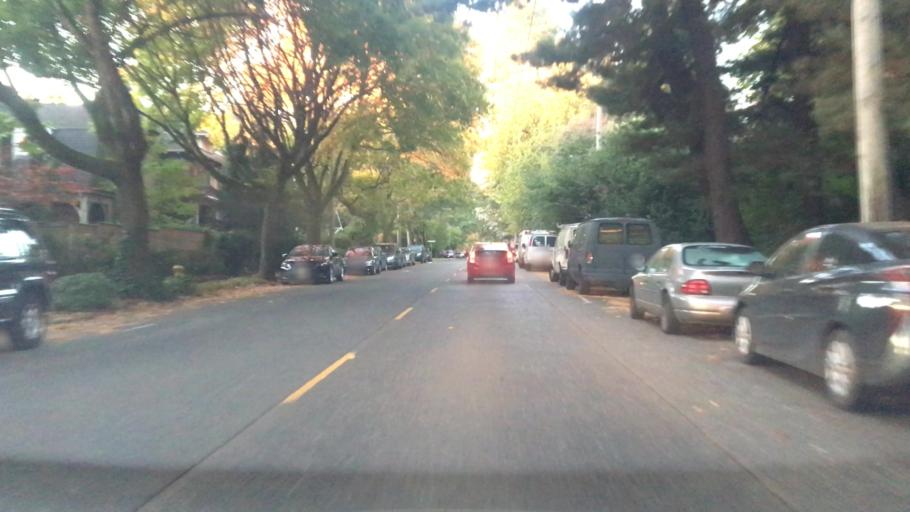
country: US
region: Washington
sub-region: King County
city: Seattle
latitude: 47.6299
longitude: -122.3126
